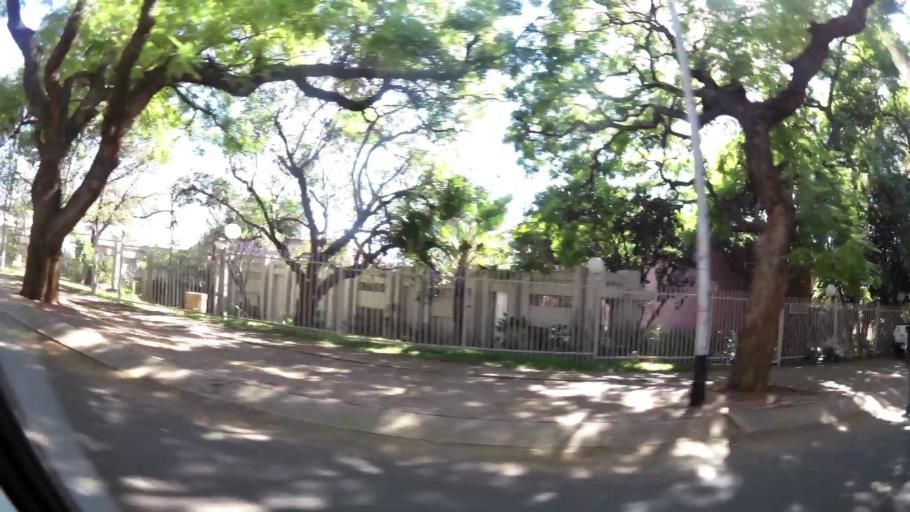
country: ZA
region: Gauteng
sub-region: City of Tshwane Metropolitan Municipality
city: Pretoria
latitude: -25.7759
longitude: 28.2318
